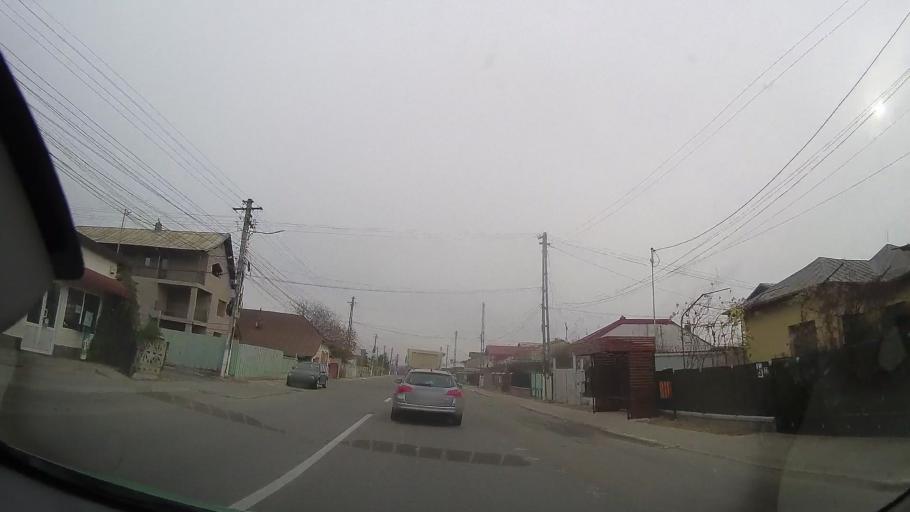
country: RO
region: Prahova
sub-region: Oras Baicoi
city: Liliesti
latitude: 45.0351
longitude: 25.8946
